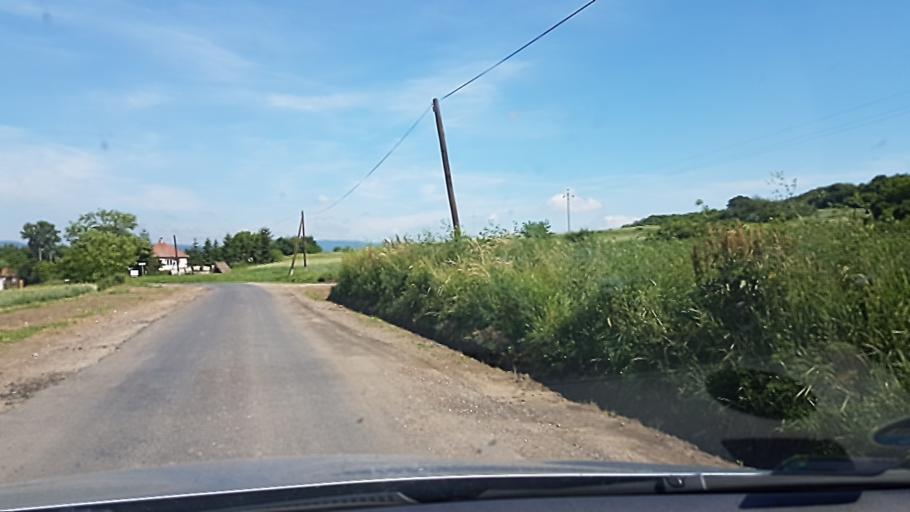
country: HU
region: Borsod-Abauj-Zemplen
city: Saly
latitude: 47.9502
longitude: 20.6999
